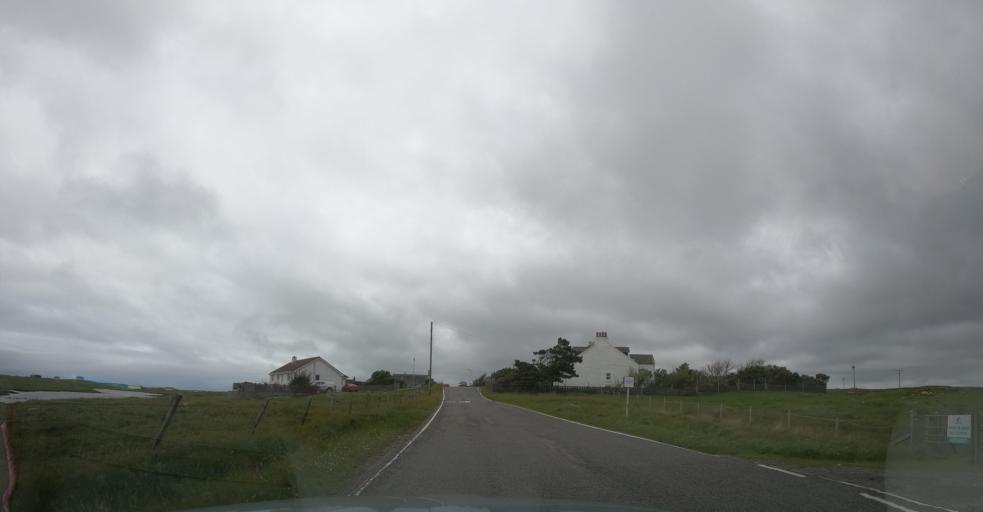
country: GB
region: Scotland
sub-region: Eilean Siar
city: Isle of North Uist
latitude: 57.5504
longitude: -7.3299
